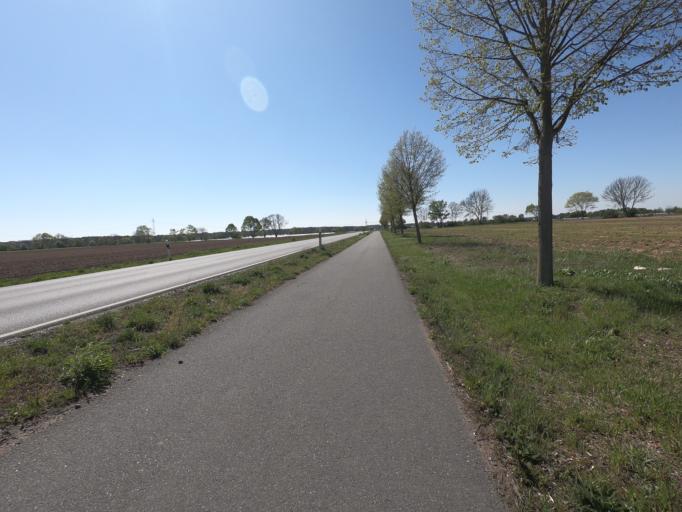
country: DE
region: Hesse
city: Weiterstadt
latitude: 49.9269
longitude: 8.6165
